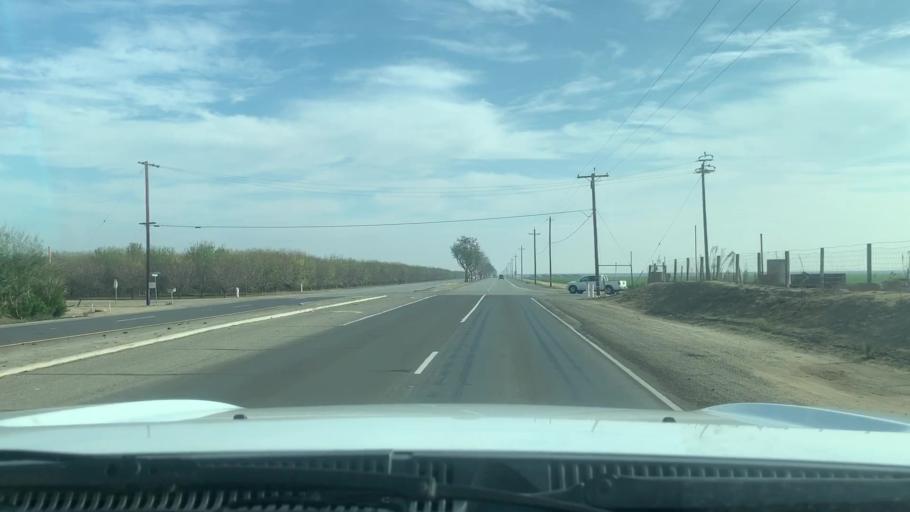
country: US
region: California
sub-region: Kern County
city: Shafter
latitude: 35.4997
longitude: -119.2434
